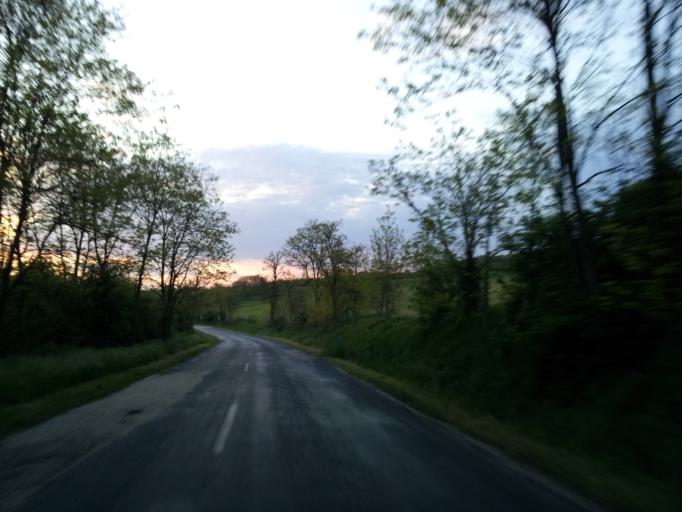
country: HU
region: Pest
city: Perbal
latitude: 47.6372
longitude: 18.7537
